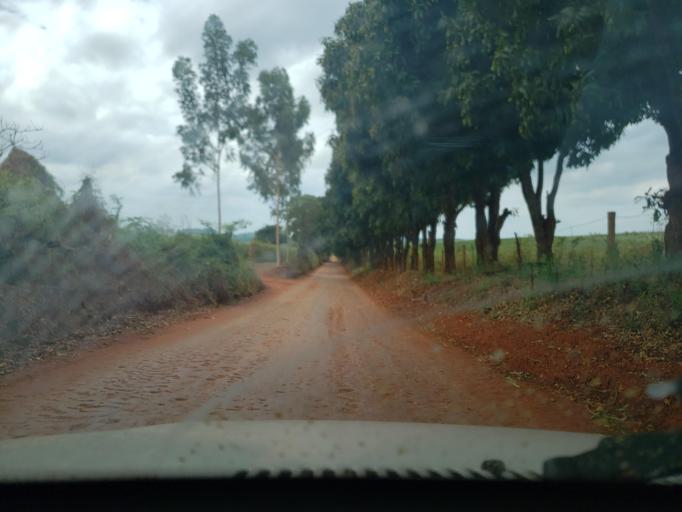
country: BR
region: Minas Gerais
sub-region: Boa Esperanca
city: Boa Esperanca
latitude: -20.9906
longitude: -45.5968
